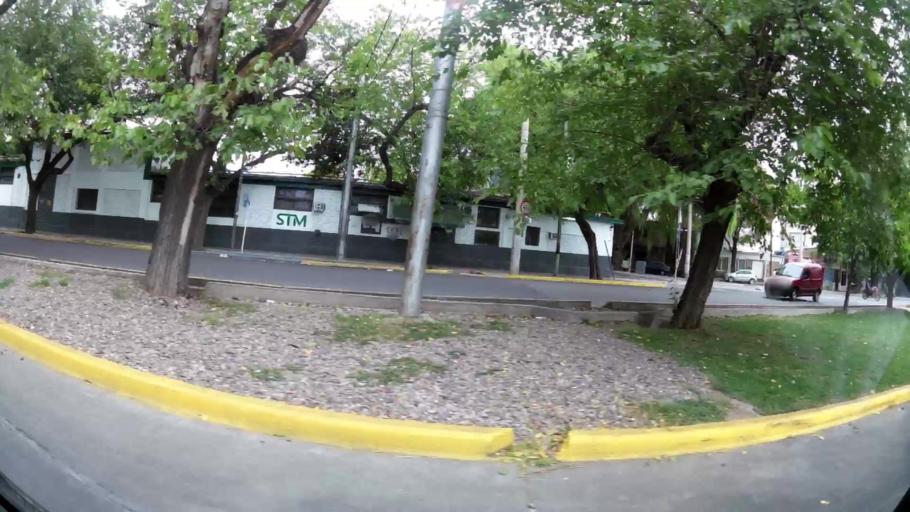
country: AR
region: Mendoza
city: Mendoza
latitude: -32.8733
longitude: -68.8440
